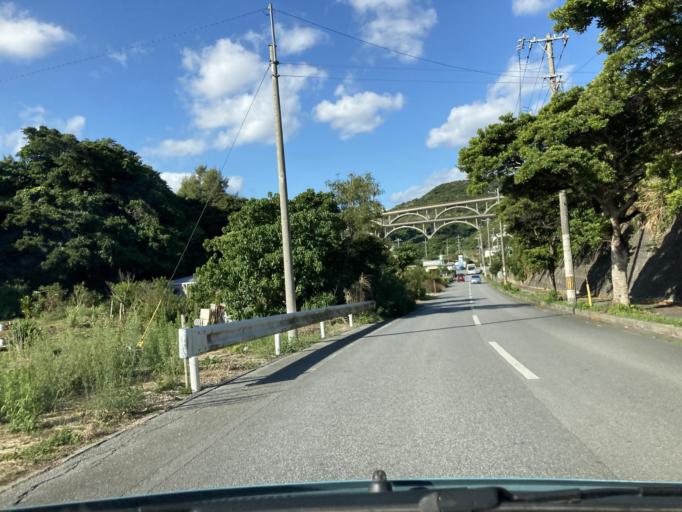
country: JP
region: Okinawa
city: Ginowan
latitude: 26.2155
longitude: 127.7442
